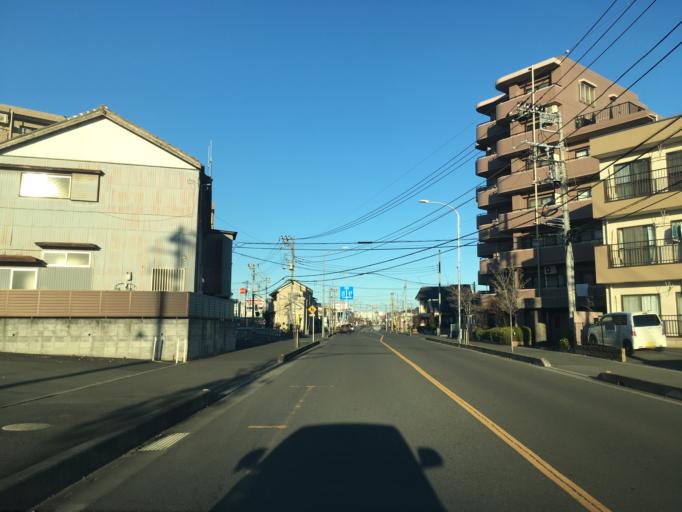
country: JP
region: Saitama
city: Sayama
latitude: 35.8219
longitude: 139.3998
